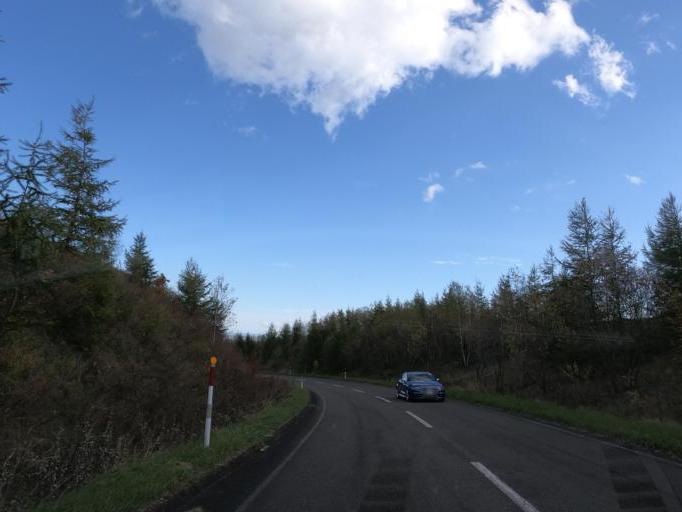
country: JP
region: Hokkaido
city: Otofuke
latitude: 43.2768
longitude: 143.2352
